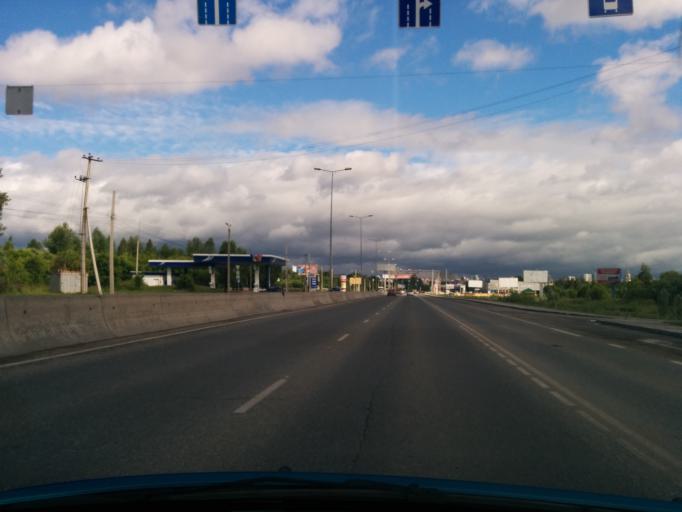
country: RU
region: Perm
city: Perm
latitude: 58.0320
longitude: 56.2100
